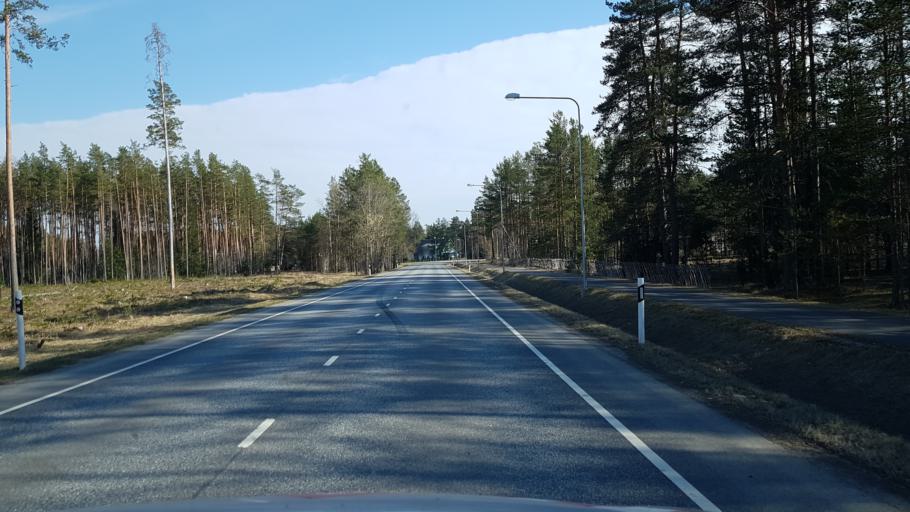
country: EE
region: Laeaene-Virumaa
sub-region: Kadrina vald
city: Kadrina
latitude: 59.4585
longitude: 26.0074
